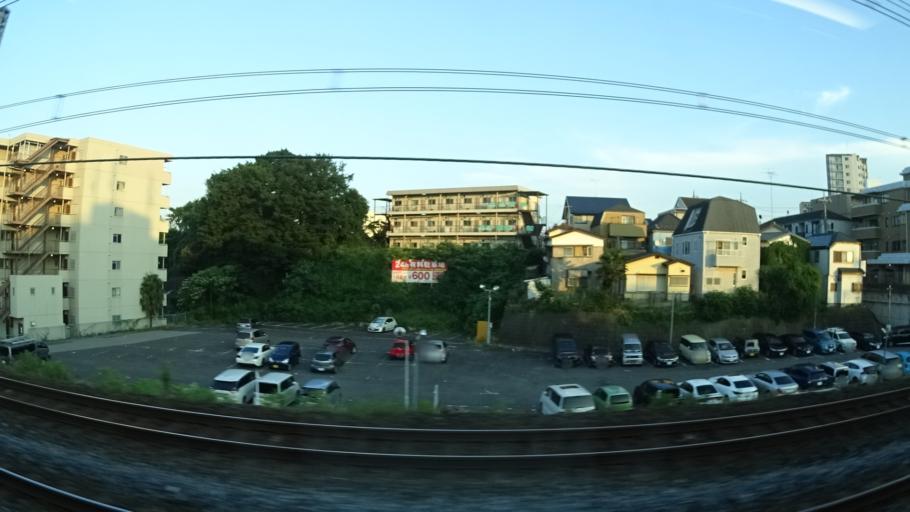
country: JP
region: Chiba
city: Nagareyama
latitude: 35.8347
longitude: 139.9336
